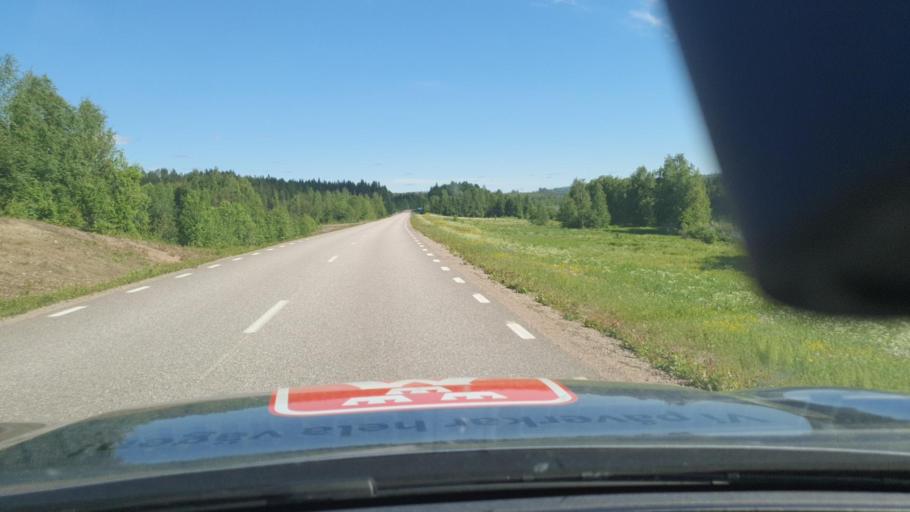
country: SE
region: Norrbotten
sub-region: Overkalix Kommun
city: OEverkalix
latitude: 66.7717
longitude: 22.6911
